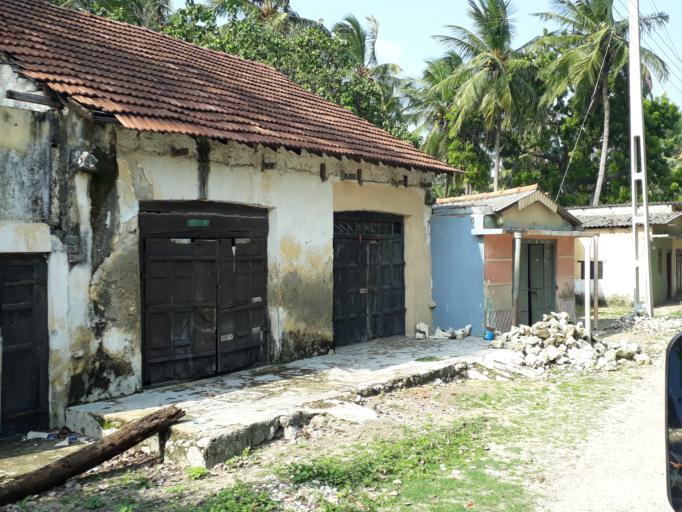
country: LK
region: Northern Province
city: Jaffna
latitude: 9.5276
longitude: 79.7160
